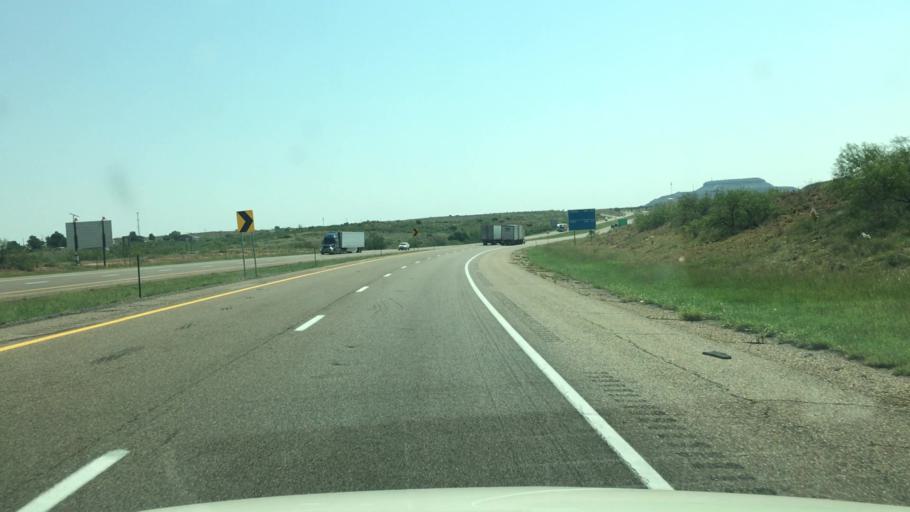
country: US
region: New Mexico
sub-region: Quay County
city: Tucumcari
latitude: 35.1566
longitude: -103.7620
